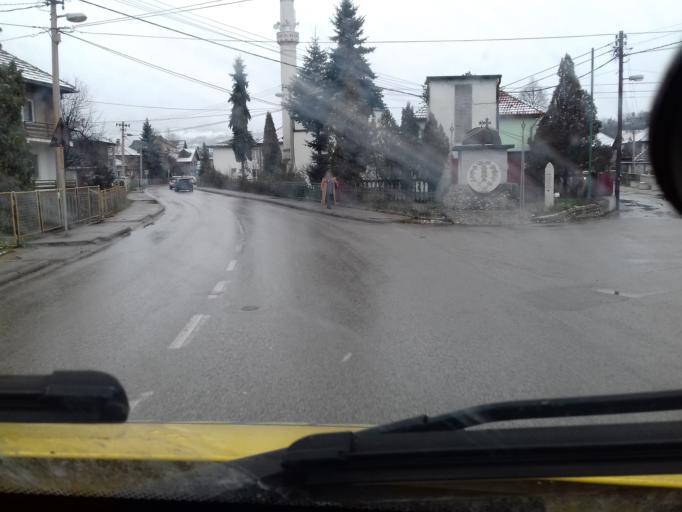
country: BA
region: Federation of Bosnia and Herzegovina
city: Kakanj
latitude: 44.1140
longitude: 18.1176
